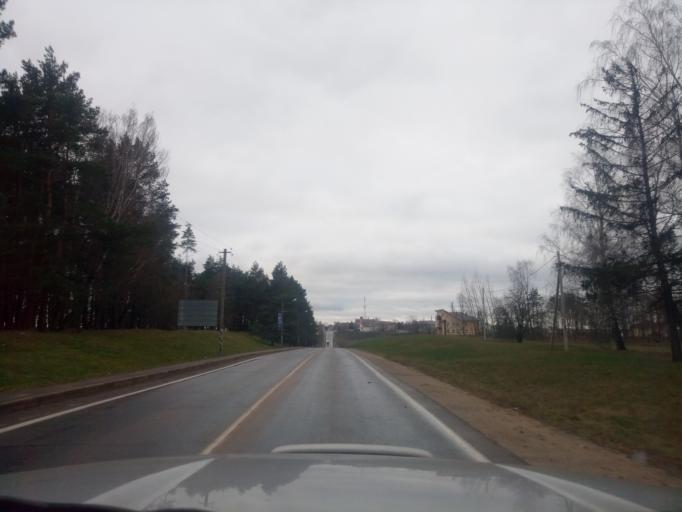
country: BY
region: Minsk
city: Kapyl'
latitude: 53.1555
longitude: 27.1008
